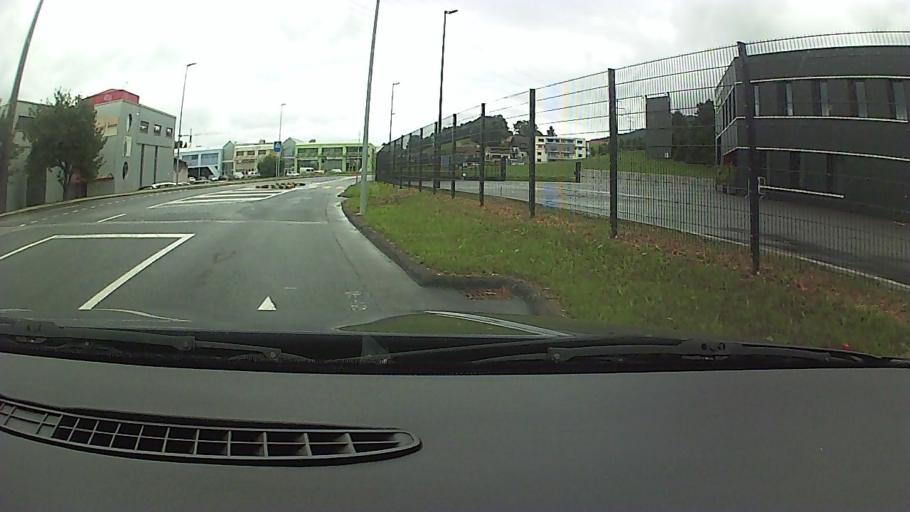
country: CH
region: Fribourg
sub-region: Veveyse District
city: Chatel-Saint-Denis
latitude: 46.5211
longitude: 6.9051
